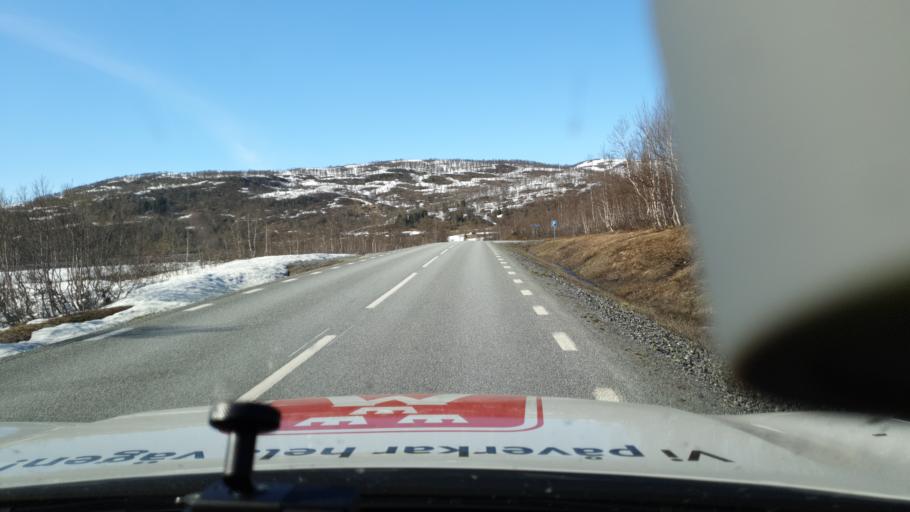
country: NO
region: Nordland
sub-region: Rana
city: Mo i Rana
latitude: 66.0948
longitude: 14.8512
